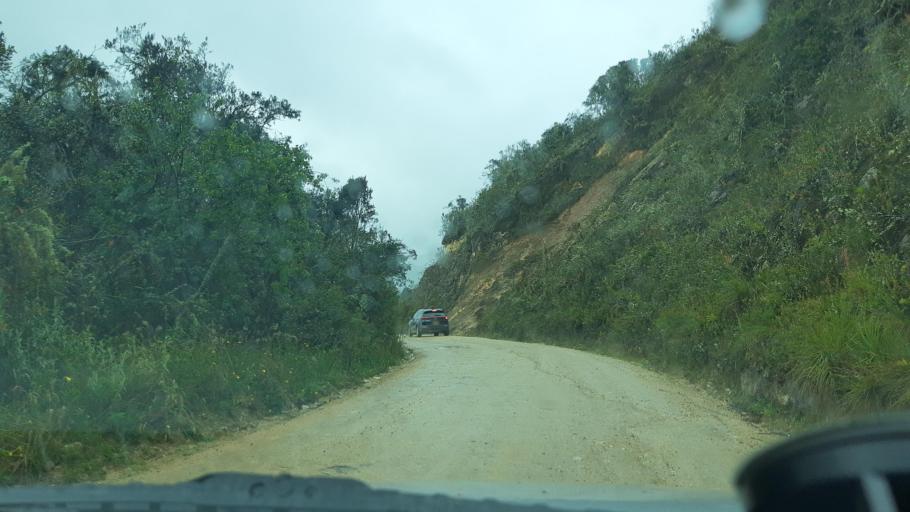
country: CO
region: Cundinamarca
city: Villapinzon
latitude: 5.2120
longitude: -73.5733
